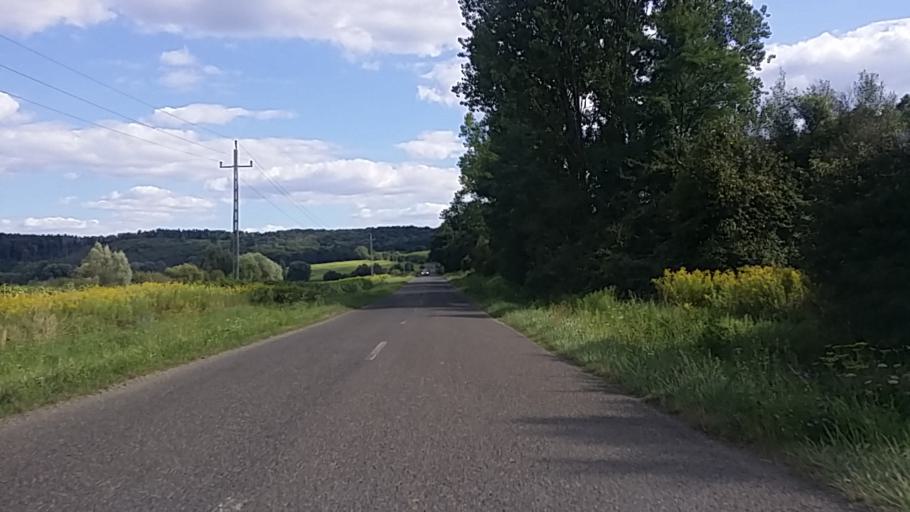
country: HU
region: Baranya
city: Sasd
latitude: 46.1649
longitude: 18.0900
